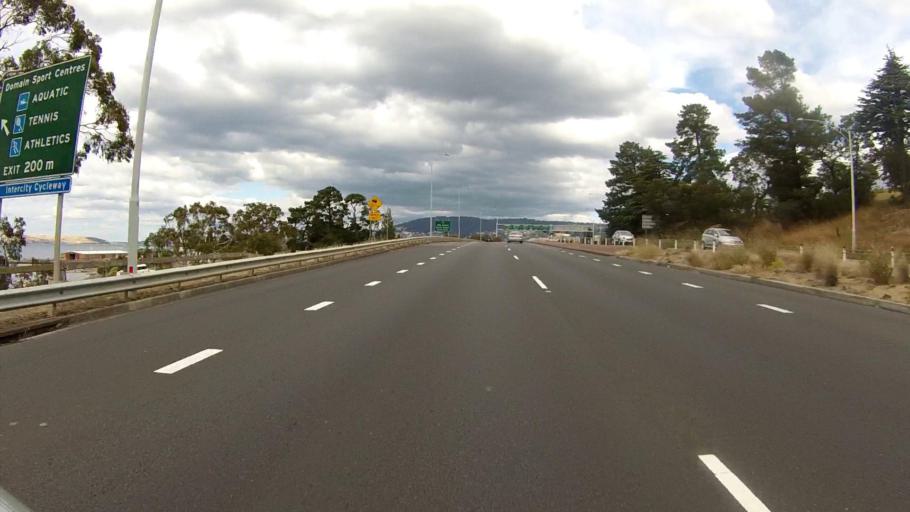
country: AU
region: Tasmania
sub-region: Hobart
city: Hobart
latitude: -42.8733
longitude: 147.3342
